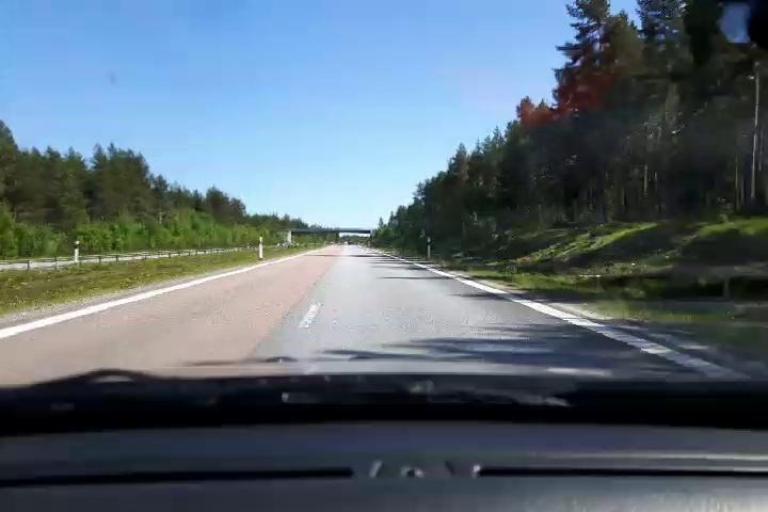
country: SE
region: Gaevleborg
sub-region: Soderhamns Kommun
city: Soderhamn
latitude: 61.3737
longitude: 17.0001
